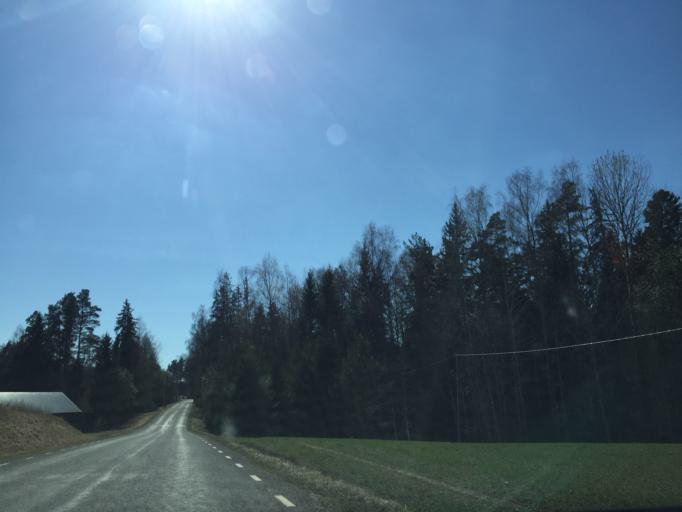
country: EE
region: Viljandimaa
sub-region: Viljandi linn
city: Viljandi
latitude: 58.2883
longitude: 25.5869
